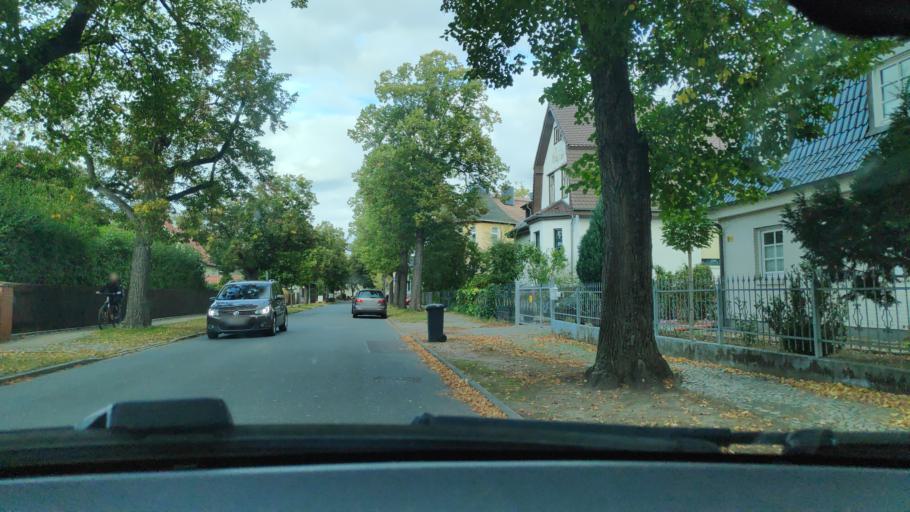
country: DE
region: Saxony-Anhalt
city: Biederitz
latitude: 52.1548
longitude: 11.7138
